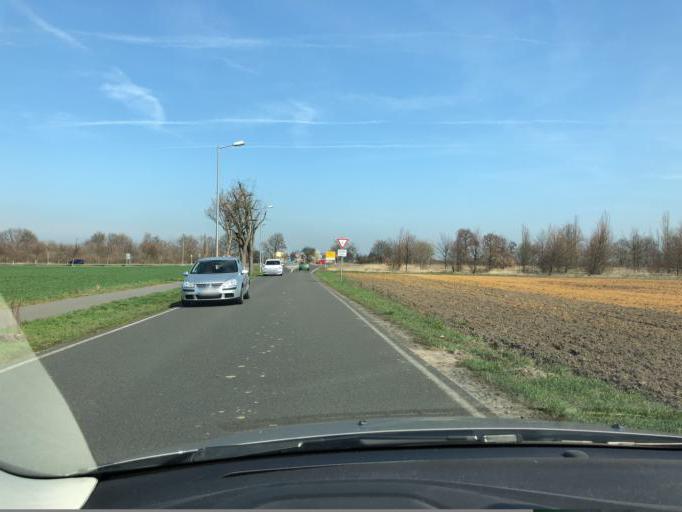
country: DE
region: Saxony
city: Rackwitz
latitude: 51.4126
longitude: 12.4202
